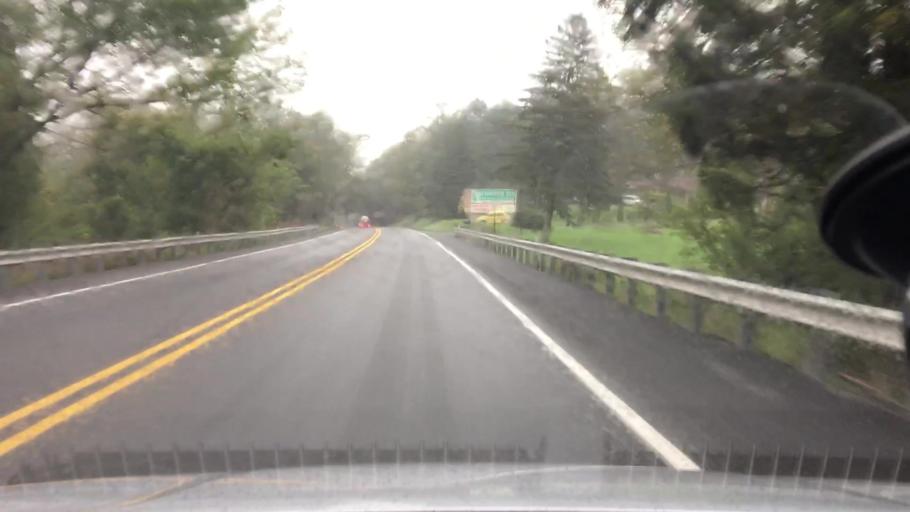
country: US
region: Pennsylvania
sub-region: Monroe County
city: Mount Pocono
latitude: 41.1281
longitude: -75.3206
